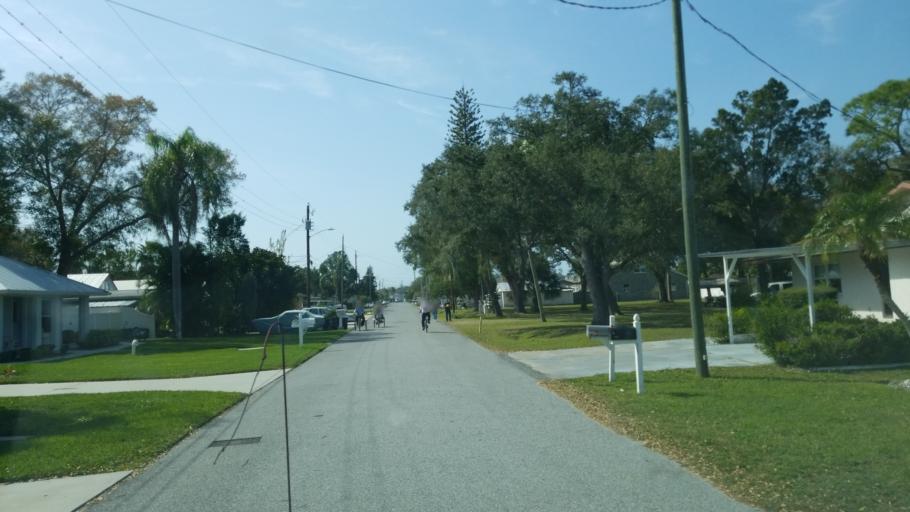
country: US
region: Florida
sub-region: Sarasota County
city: Southgate
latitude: 27.3212
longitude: -82.4982
